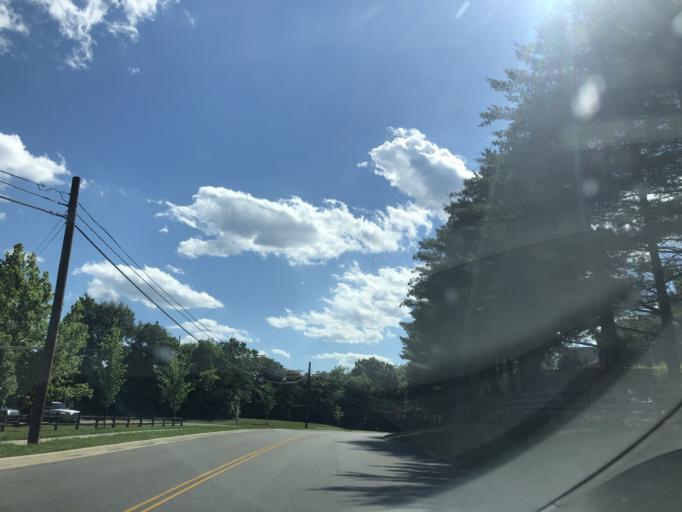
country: US
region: Tennessee
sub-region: Davidson County
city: Belle Meade
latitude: 36.0627
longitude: -86.9180
